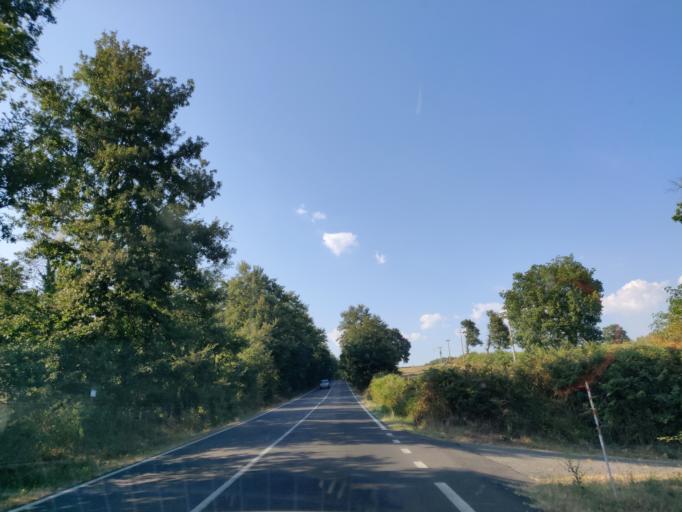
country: IT
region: Latium
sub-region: Provincia di Viterbo
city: Latera
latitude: 42.6075
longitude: 11.8436
